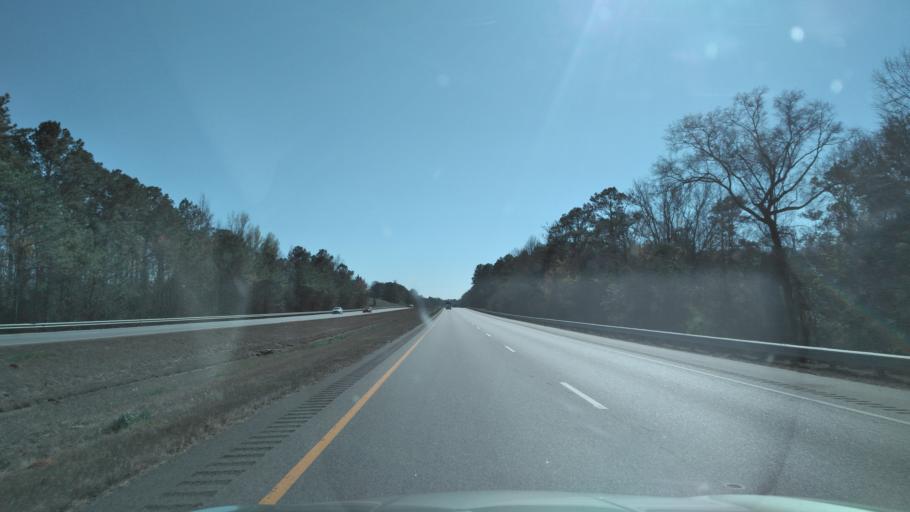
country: US
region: Alabama
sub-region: Lowndes County
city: Fort Deposit
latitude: 31.9281
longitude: -86.5732
